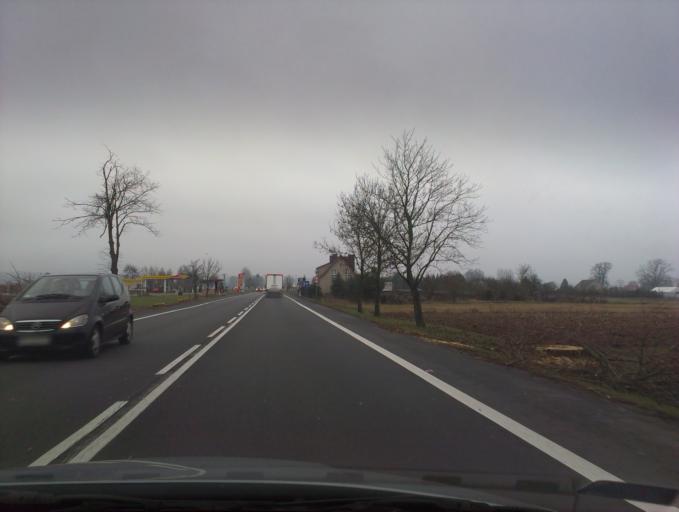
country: PL
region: Greater Poland Voivodeship
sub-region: Powiat pilski
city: Ujscie
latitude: 53.0766
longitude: 16.7315
